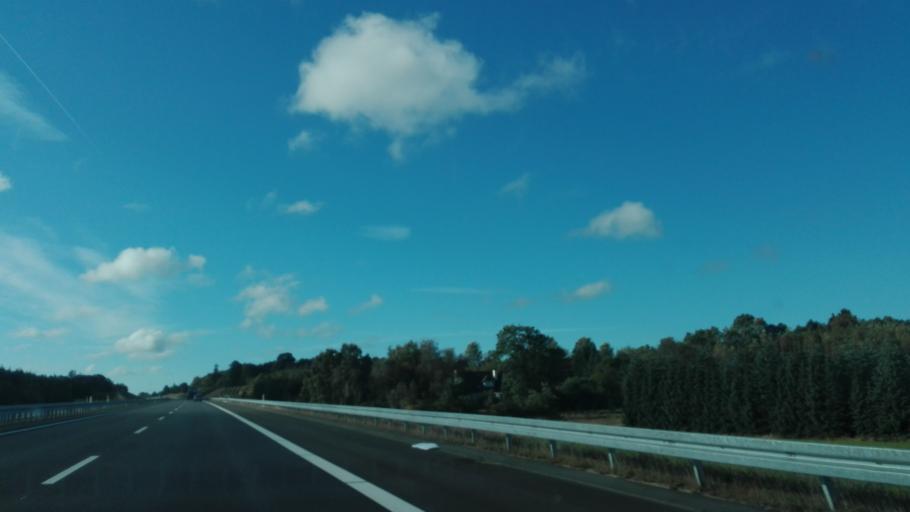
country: DK
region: Central Jutland
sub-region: Silkeborg Kommune
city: Silkeborg
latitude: 56.1832
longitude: 9.4862
